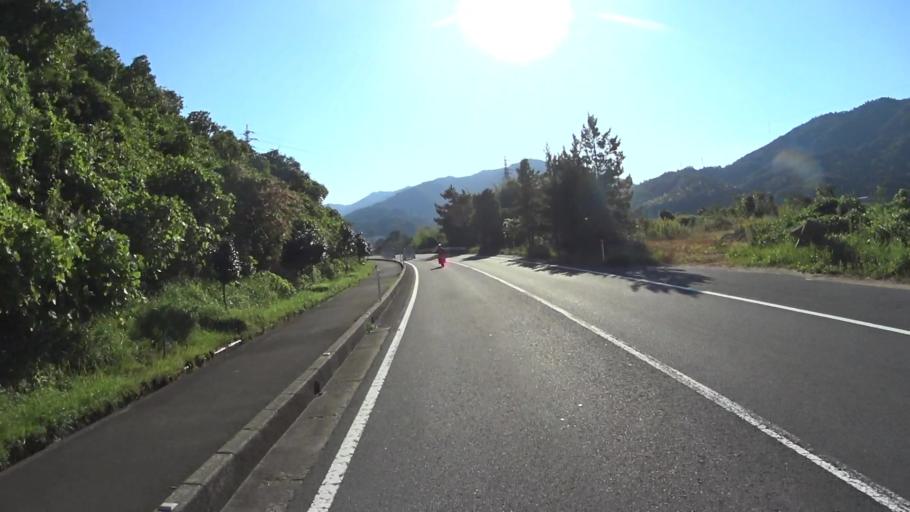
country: JP
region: Kyoto
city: Miyazu
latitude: 35.4870
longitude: 135.0956
